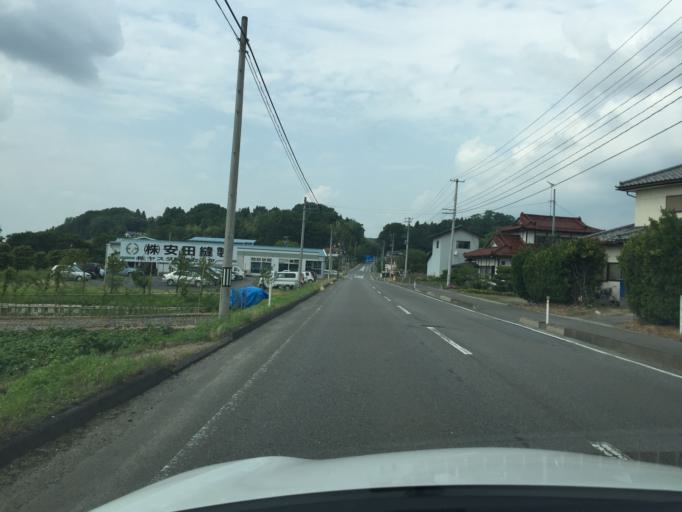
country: JP
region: Fukushima
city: Sukagawa
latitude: 37.2717
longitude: 140.4193
